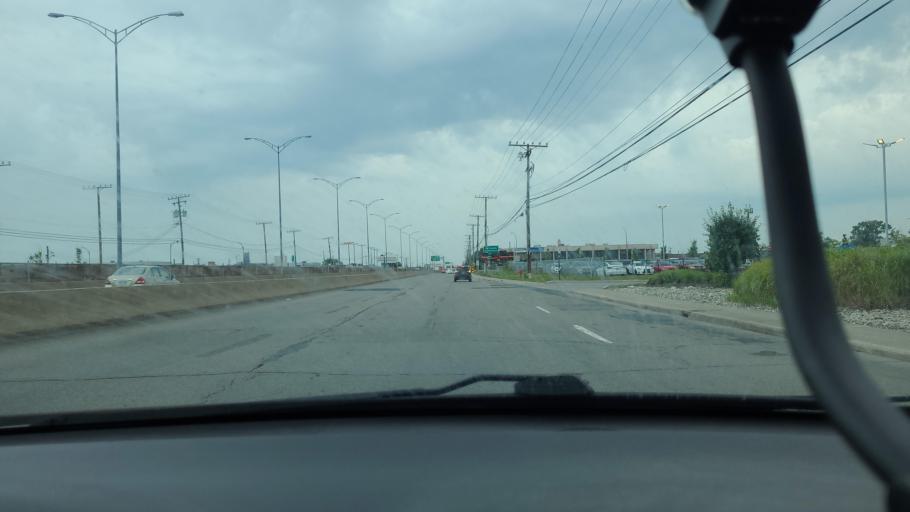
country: CA
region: Quebec
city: Cote-Saint-Luc
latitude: 45.4750
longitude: -73.7062
